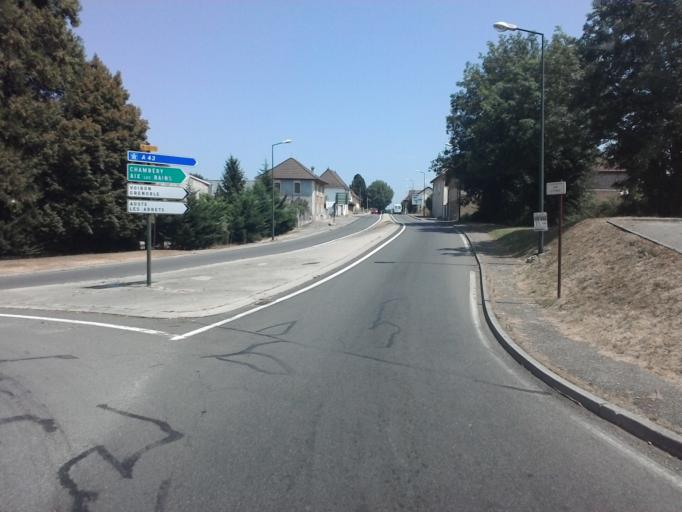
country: FR
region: Rhone-Alpes
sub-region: Departement de l'Isere
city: La Batie-Montgascon
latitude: 45.5834
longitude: 5.5438
